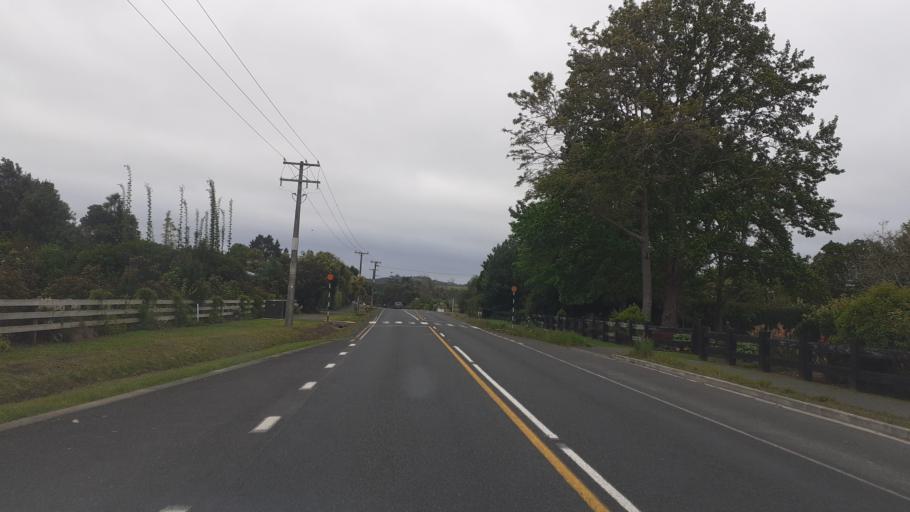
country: NZ
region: Northland
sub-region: Far North District
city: Kerikeri
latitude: -35.2079
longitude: 173.9645
